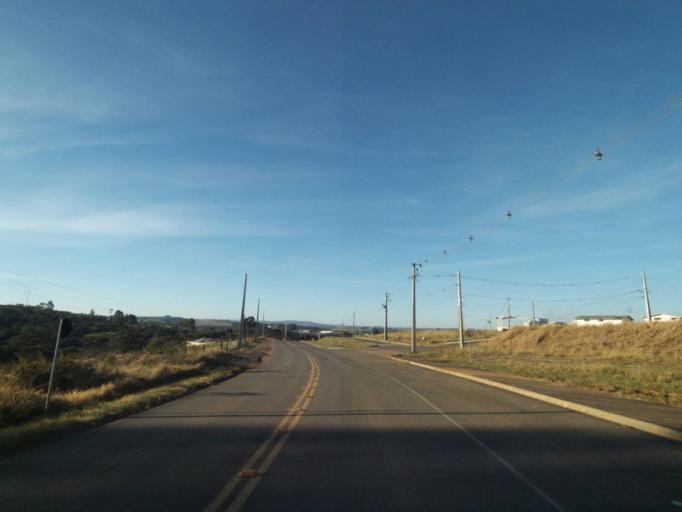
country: BR
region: Parana
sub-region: Tibagi
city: Tibagi
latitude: -24.5206
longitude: -50.4263
